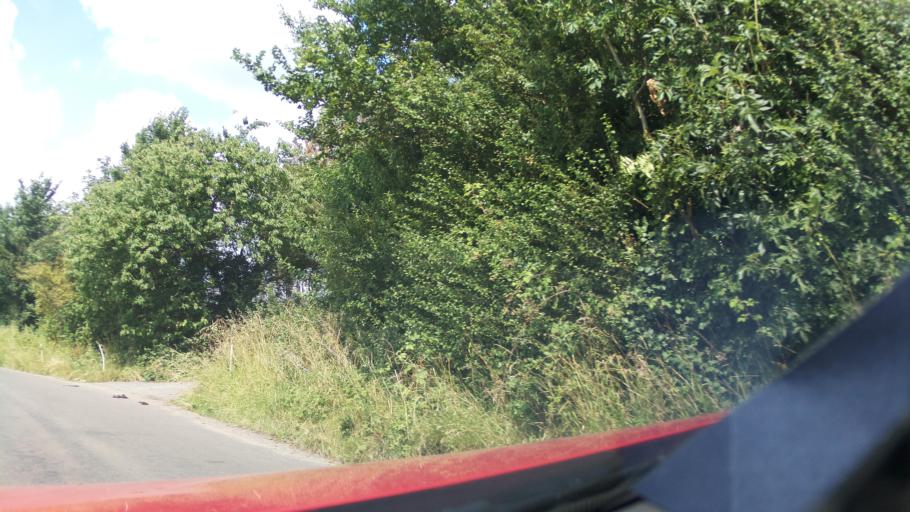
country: GB
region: England
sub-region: Wiltshire
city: Hankerton
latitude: 51.6232
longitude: -2.0500
